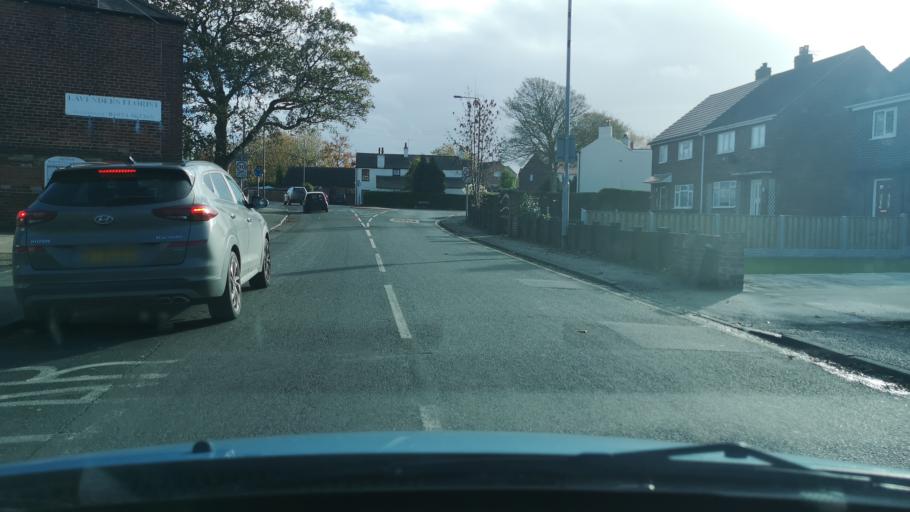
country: GB
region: England
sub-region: City and Borough of Wakefield
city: Crofton
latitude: 53.6551
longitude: -1.4276
